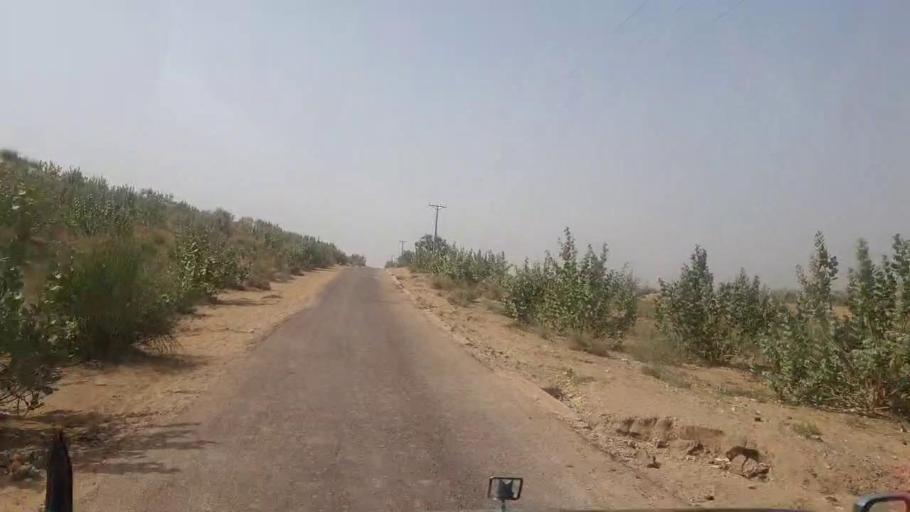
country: PK
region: Sindh
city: Islamkot
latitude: 25.1010
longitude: 70.1830
